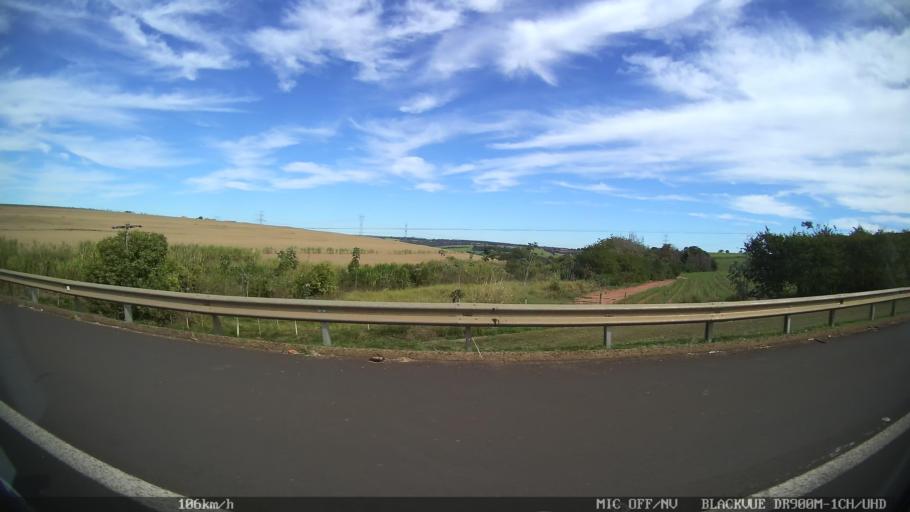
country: BR
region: Sao Paulo
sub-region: Matao
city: Matao
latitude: -21.5642
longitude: -48.4704
